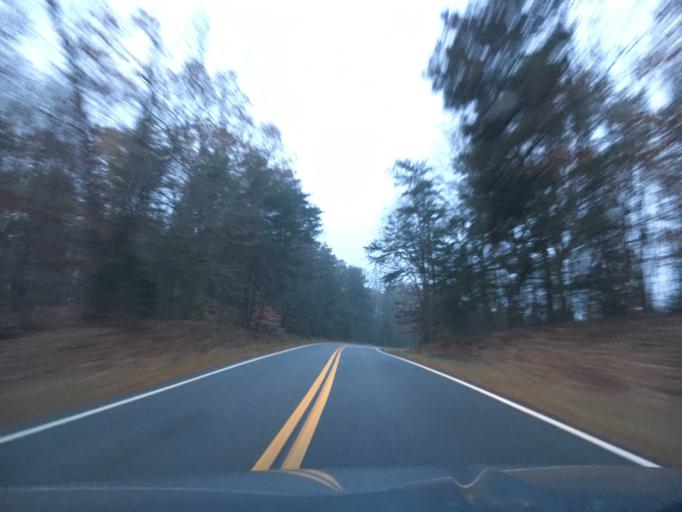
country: US
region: Virginia
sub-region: Halifax County
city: Mountain Road
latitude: 36.6911
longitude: -78.9812
